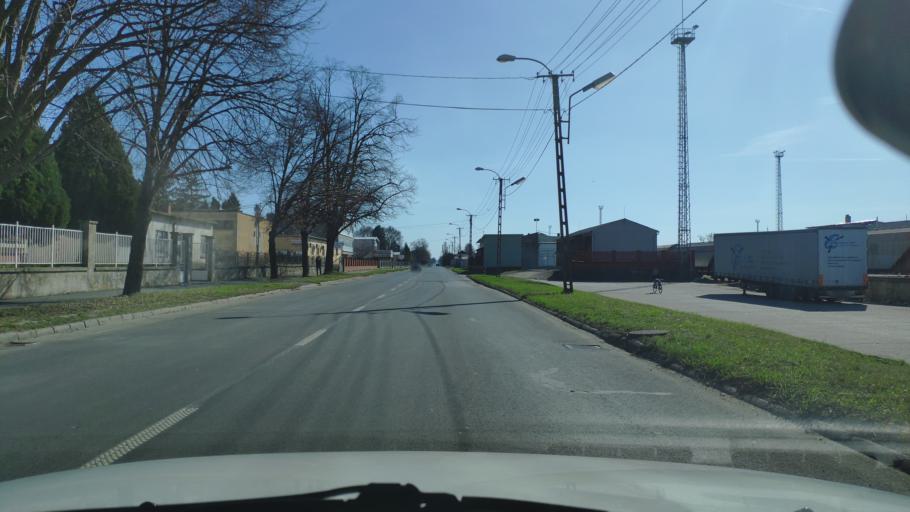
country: HU
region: Zala
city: Nagykanizsa
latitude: 46.4426
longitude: 16.9894
